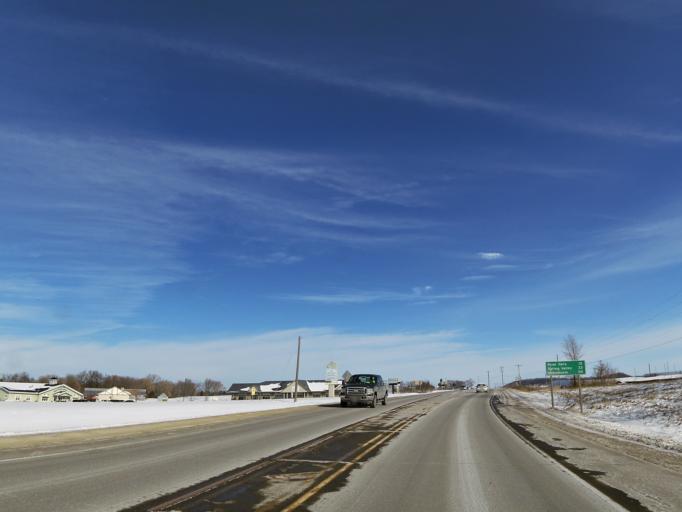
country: US
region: Wisconsin
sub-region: Pierce County
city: Prescott
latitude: 44.7622
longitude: -92.7912
